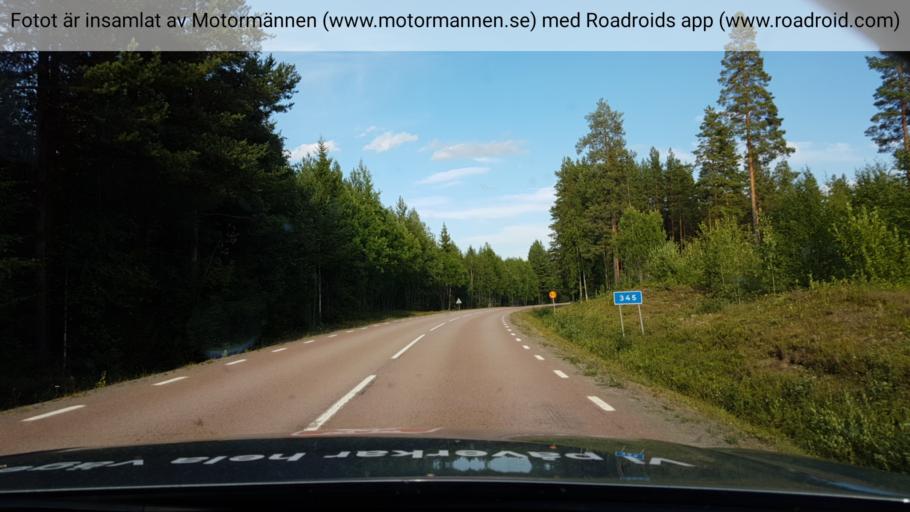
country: SE
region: Vaesternorrland
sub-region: Solleftea Kommun
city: As
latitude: 63.6003
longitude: 16.2123
